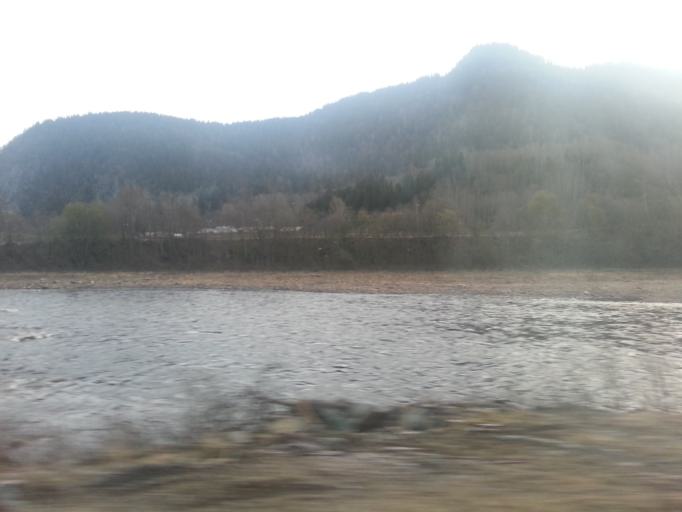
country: NO
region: Sor-Trondelag
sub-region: Midtre Gauldal
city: Storen
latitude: 63.0692
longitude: 10.2650
